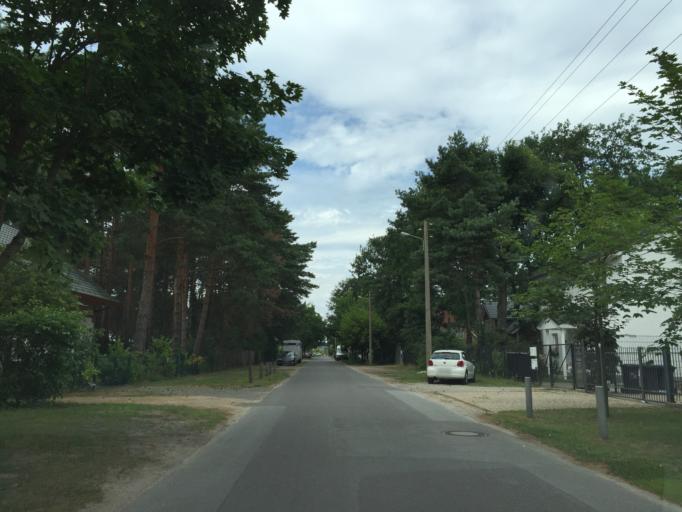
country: DE
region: Berlin
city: Mahlsdorf
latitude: 52.4896
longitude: 13.6173
